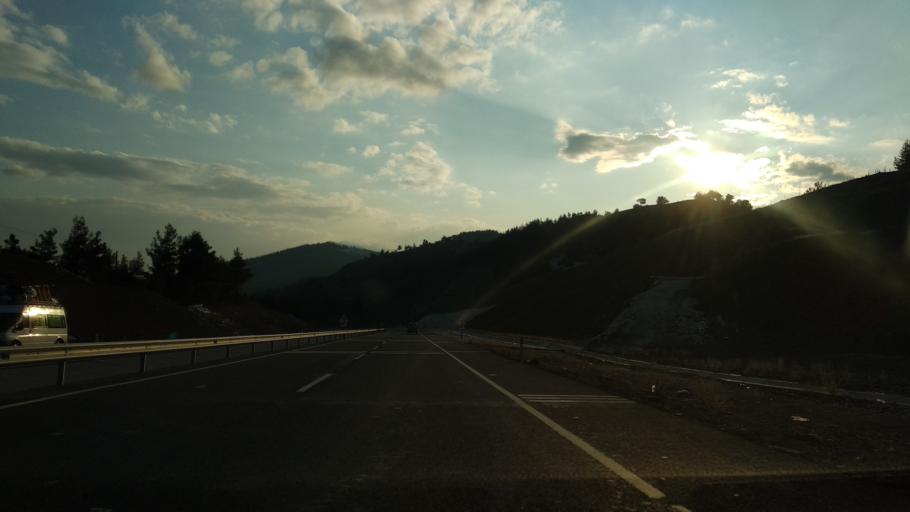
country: TR
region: Kahramanmaras
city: Yenicekale
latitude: 37.7105
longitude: 36.6917
